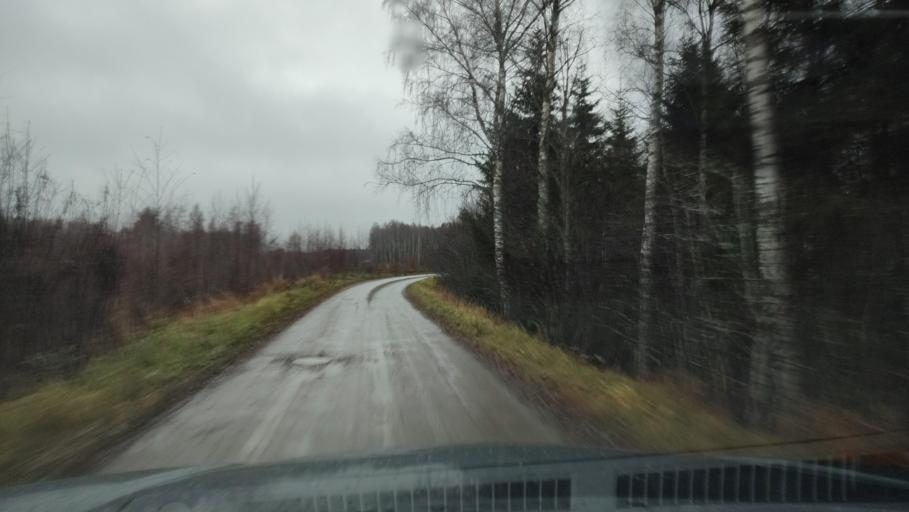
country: FI
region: Ostrobothnia
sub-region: Sydosterbotten
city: Kristinestad
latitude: 62.2381
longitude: 21.4667
